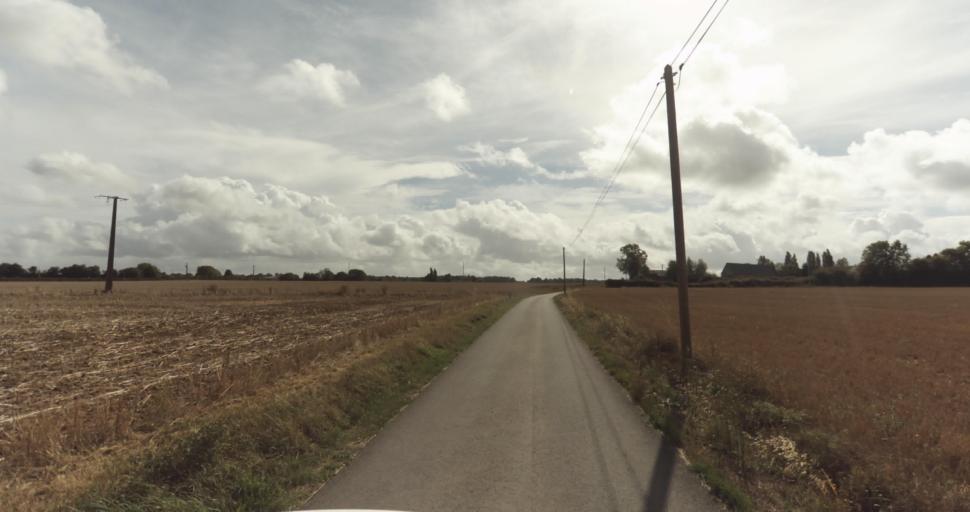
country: FR
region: Lower Normandy
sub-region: Departement de l'Orne
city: Gace
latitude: 48.8207
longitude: 0.3935
